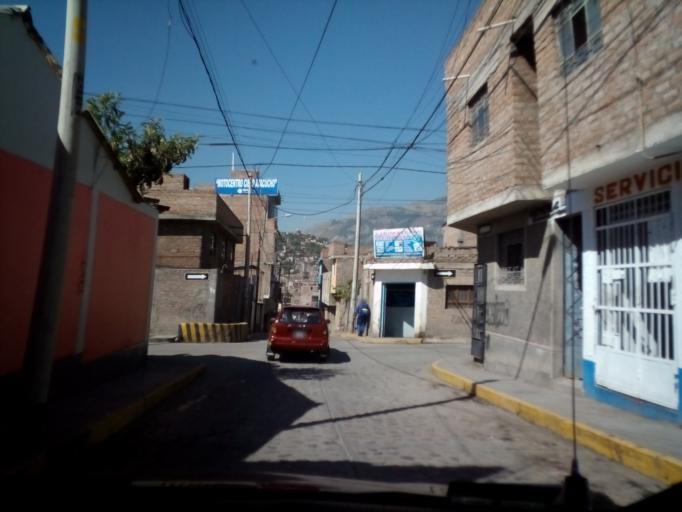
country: PE
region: Ayacucho
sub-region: Provincia de Huamanga
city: Ayacucho
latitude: -13.1591
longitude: -74.2201
